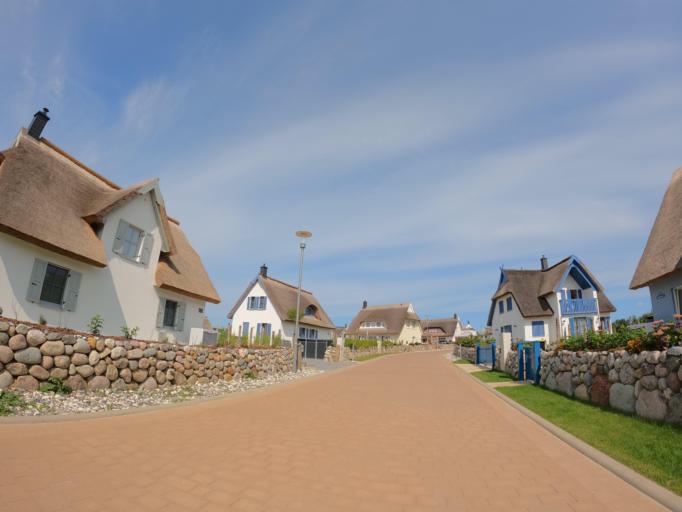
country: DE
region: Mecklenburg-Vorpommern
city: Kramerhof
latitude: 54.3513
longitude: 13.0762
